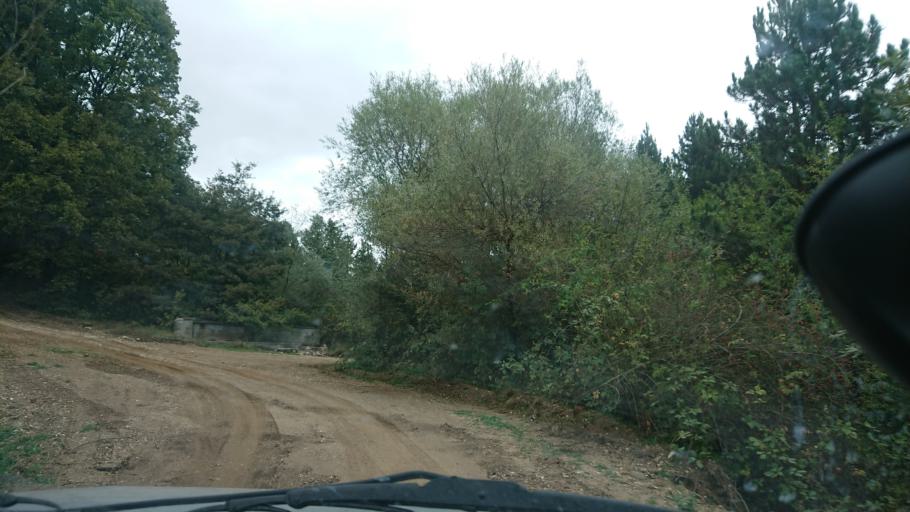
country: TR
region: Bilecik
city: Pazaryeri
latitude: 40.0172
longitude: 29.7975
